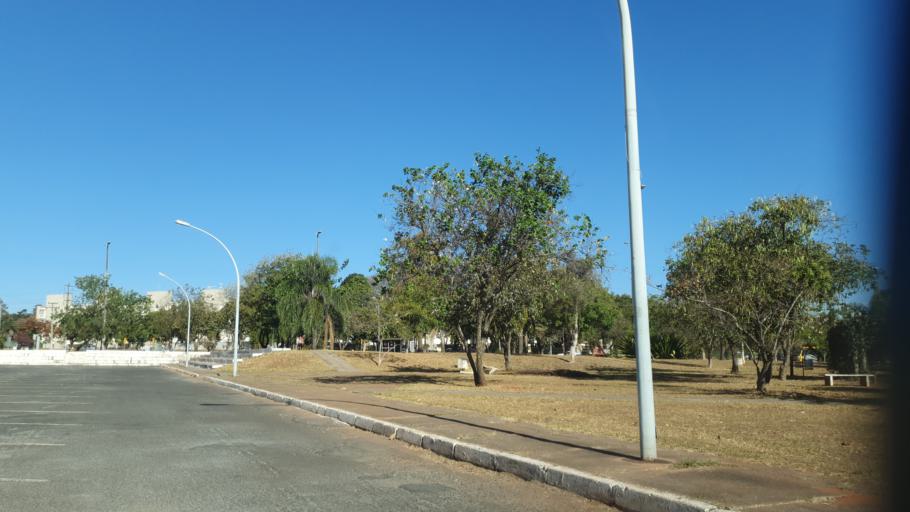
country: BR
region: Federal District
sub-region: Brasilia
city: Brasilia
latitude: -15.8011
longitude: -47.9406
